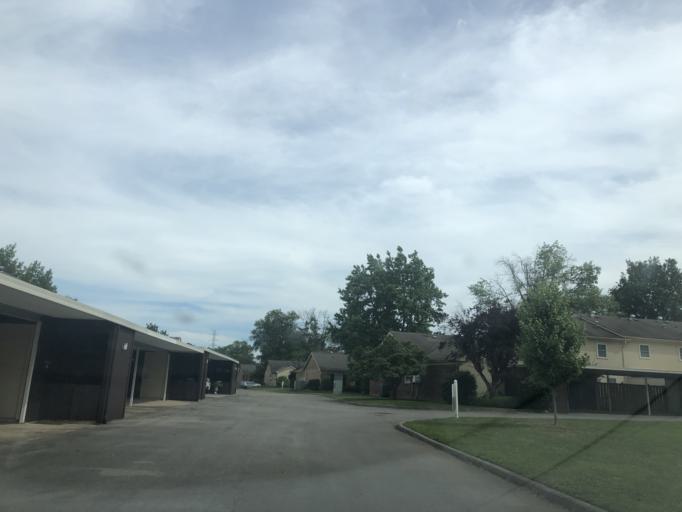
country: US
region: Tennessee
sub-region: Davidson County
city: Belle Meade
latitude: 36.0739
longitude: -86.9518
